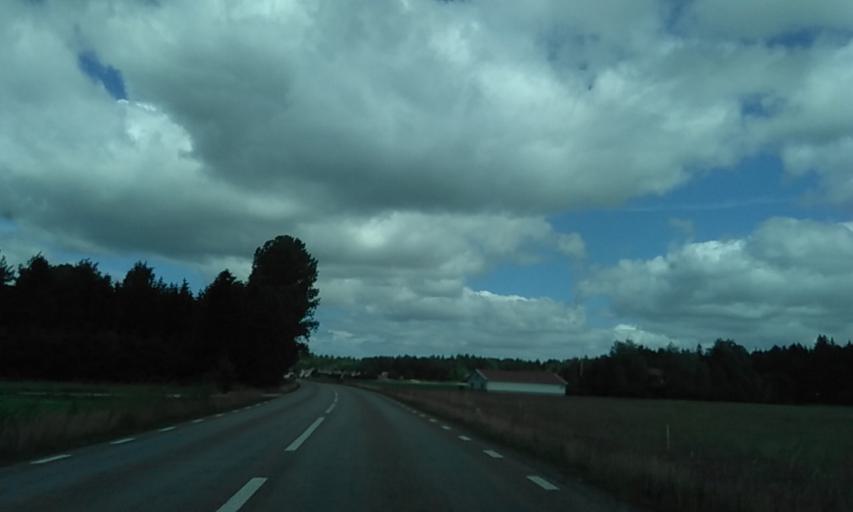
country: SE
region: Vaestra Goetaland
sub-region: Grastorps Kommun
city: Graestorp
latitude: 58.3167
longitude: 12.6741
